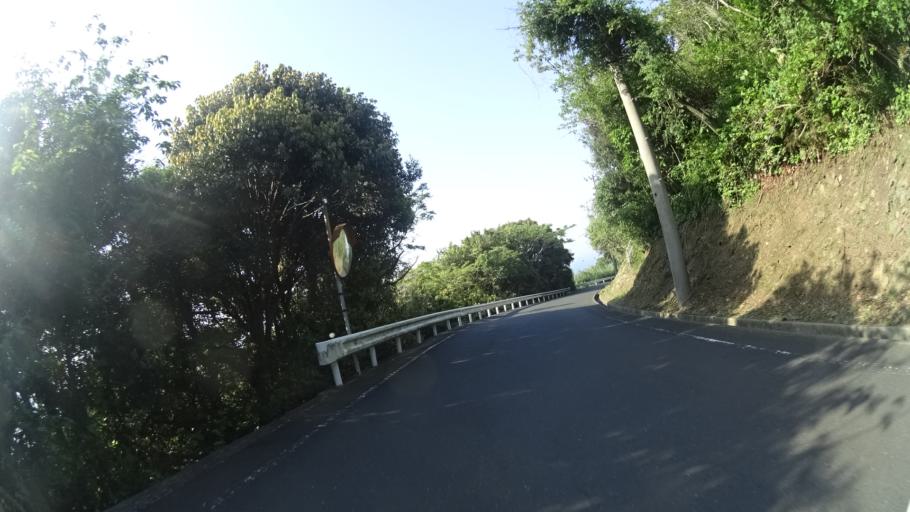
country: JP
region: Ehime
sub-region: Nishiuwa-gun
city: Ikata-cho
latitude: 33.3708
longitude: 132.0572
